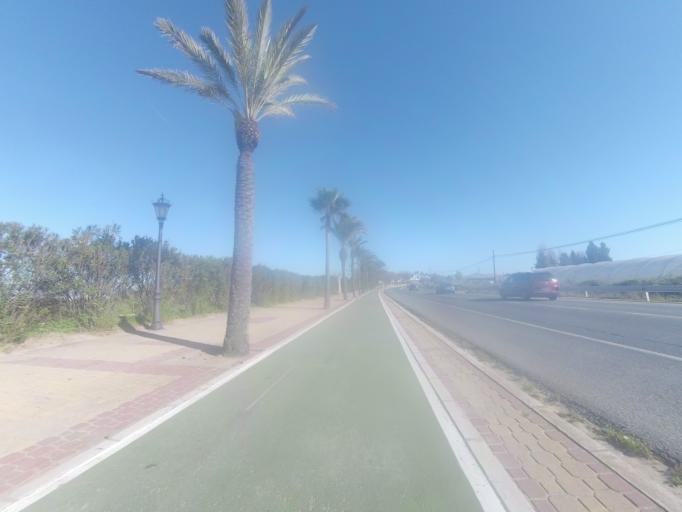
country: ES
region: Andalusia
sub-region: Provincia de Huelva
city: Palos de la Frontera
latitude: 37.2211
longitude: -6.9071
